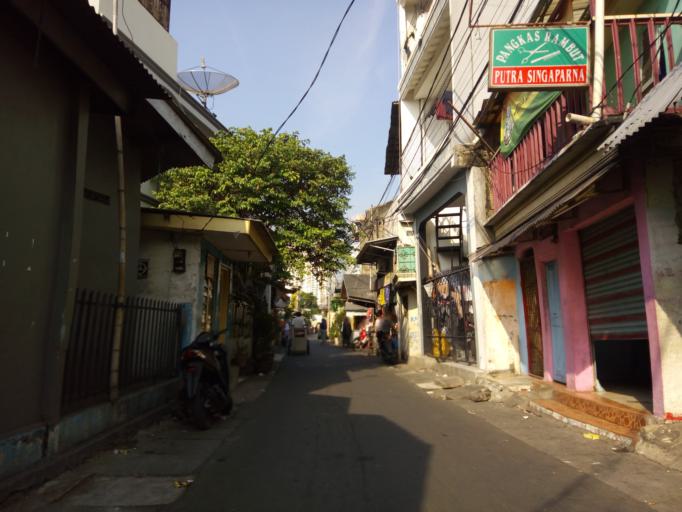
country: ID
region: Jakarta Raya
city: Jakarta
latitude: -6.2093
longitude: 106.8413
